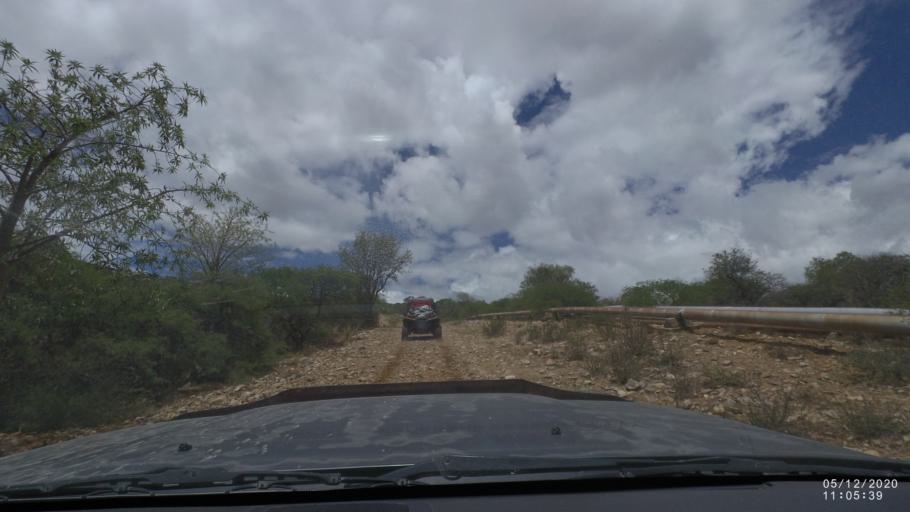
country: BO
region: Cochabamba
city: Sipe Sipe
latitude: -17.5496
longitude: -66.3041
